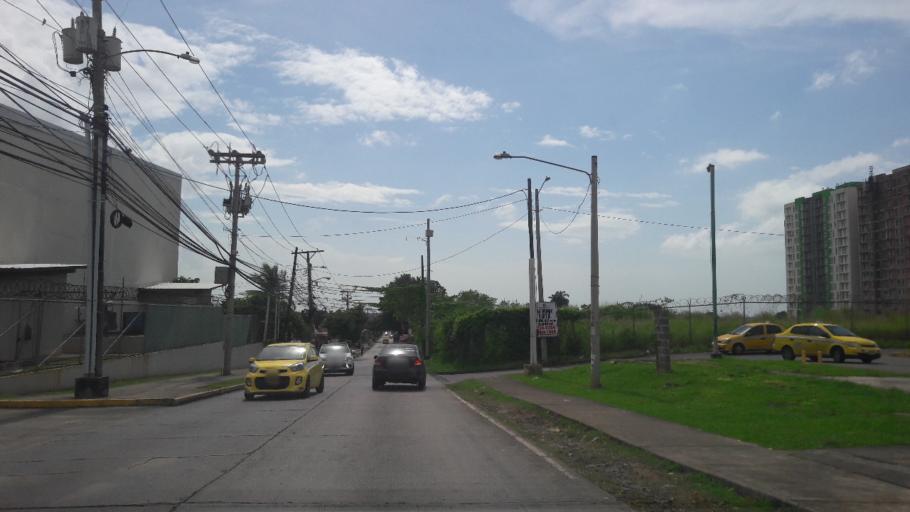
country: PA
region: Panama
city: Tocumen
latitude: 9.0615
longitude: -79.4210
